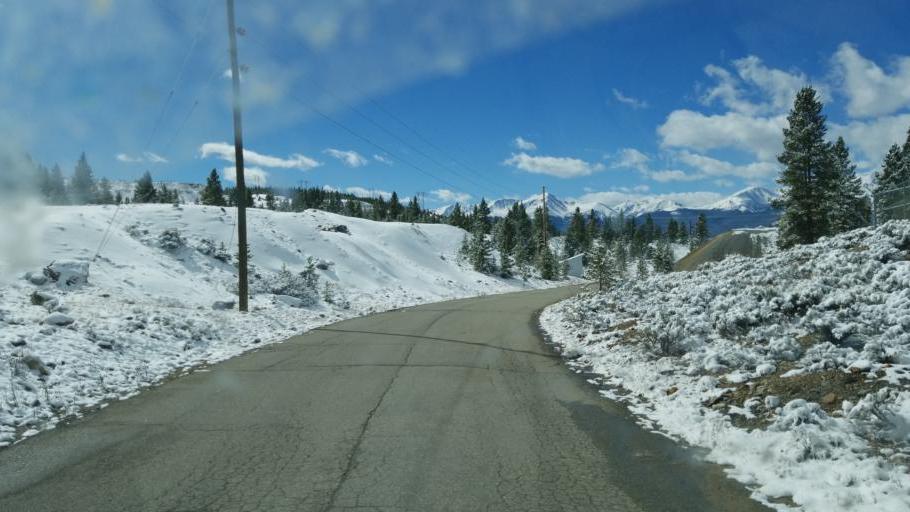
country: US
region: Colorado
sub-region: Lake County
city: Leadville
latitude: 39.2530
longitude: -106.2724
